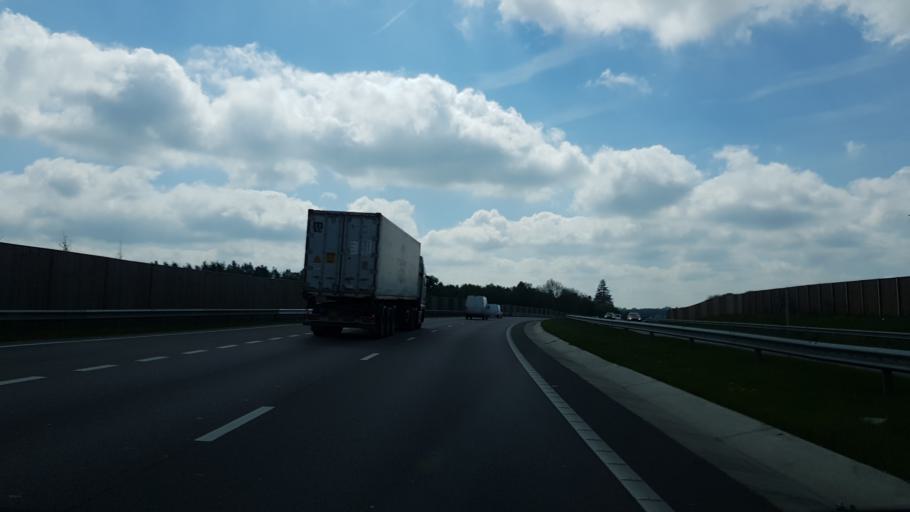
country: GB
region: England
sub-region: Kent
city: Pembury
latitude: 51.1673
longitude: 0.3054
